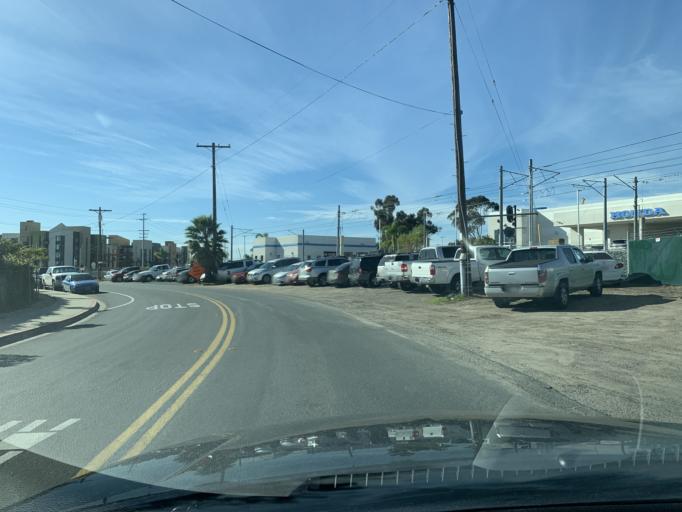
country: US
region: California
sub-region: San Diego County
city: Lemon Grove
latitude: 32.7456
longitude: -117.0288
